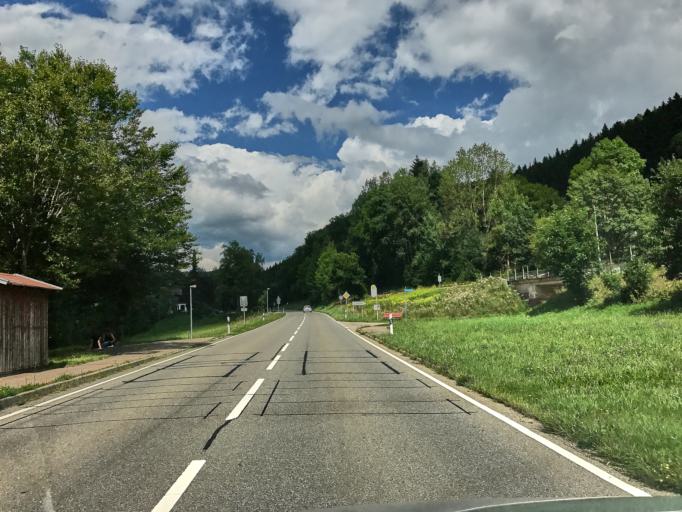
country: DE
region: Baden-Wuerttemberg
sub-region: Karlsruhe Region
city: Alpirsbach
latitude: 48.3576
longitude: 8.4137
